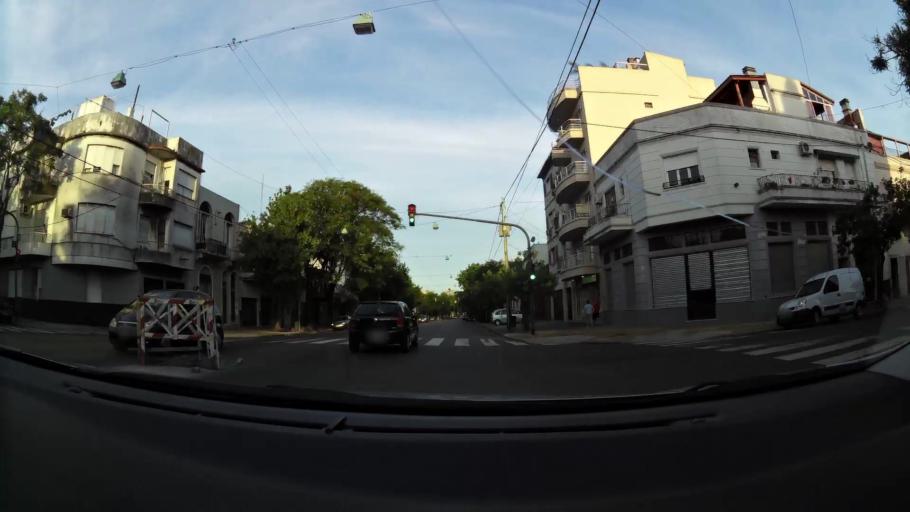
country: AR
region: Buenos Aires F.D.
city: Buenos Aires
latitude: -34.6400
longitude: -58.4224
